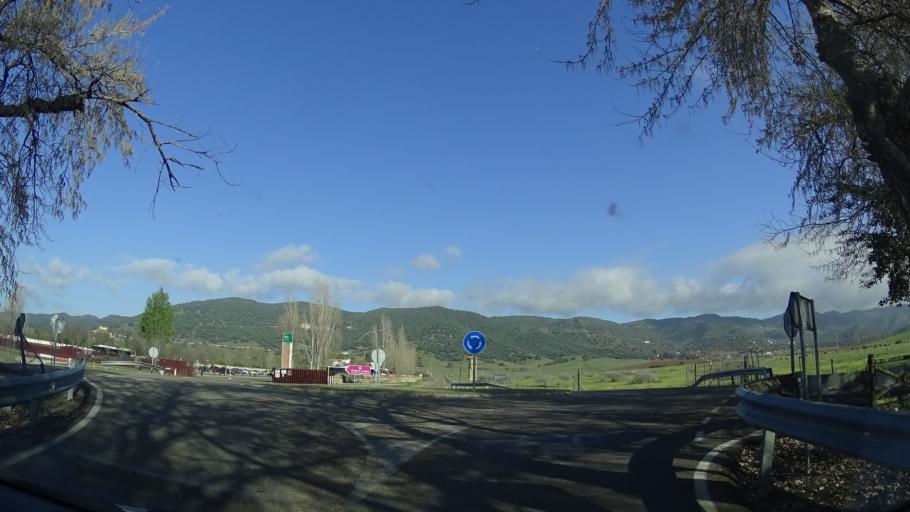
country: ES
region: Andalusia
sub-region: Province of Cordoba
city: Villarrubia
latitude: 37.8799
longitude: -4.8513
